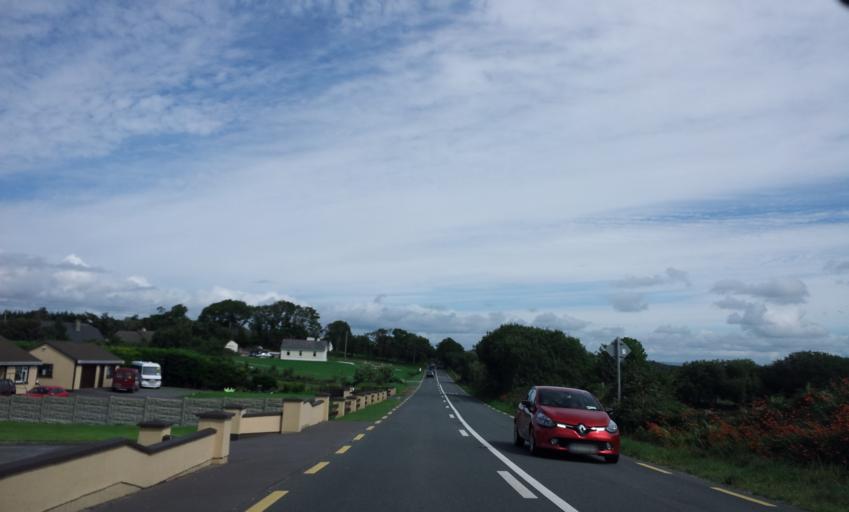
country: IE
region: Munster
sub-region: Ciarrai
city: Killorglin
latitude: 52.0928
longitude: -9.8450
